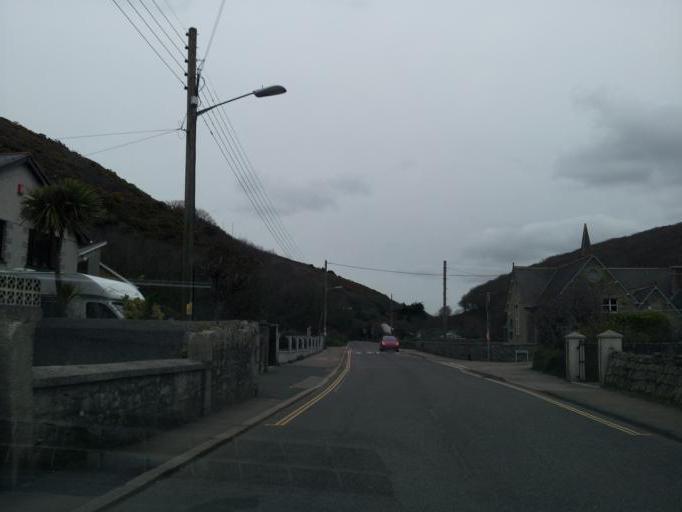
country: GB
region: England
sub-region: Cornwall
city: Camborne
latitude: 50.2606
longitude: -5.2823
